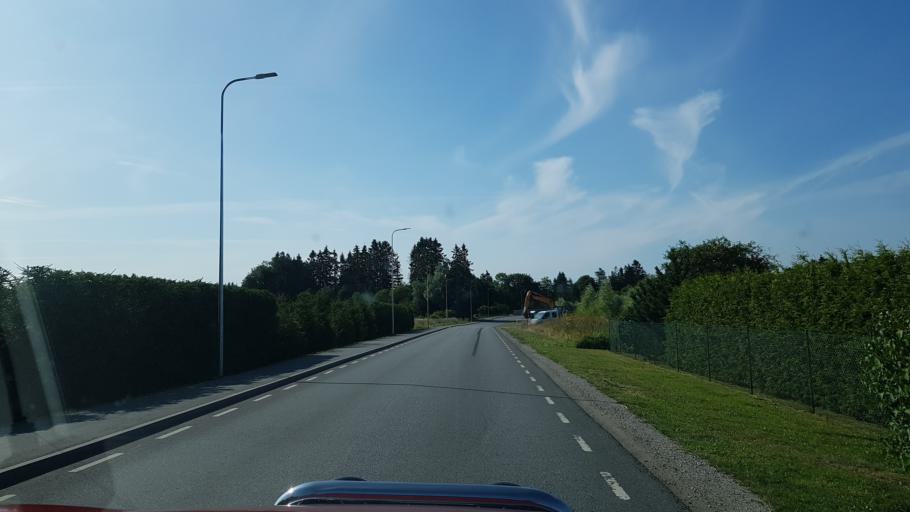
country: EE
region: Harju
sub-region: Joelaehtme vald
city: Loo
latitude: 59.3961
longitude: 24.9337
